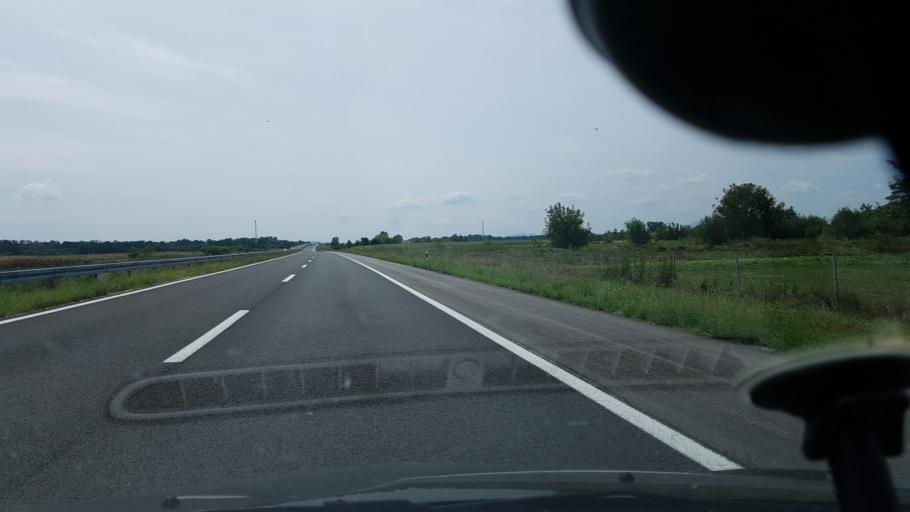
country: HR
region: Medimurska
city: Palovec
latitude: 46.3864
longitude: 16.5581
